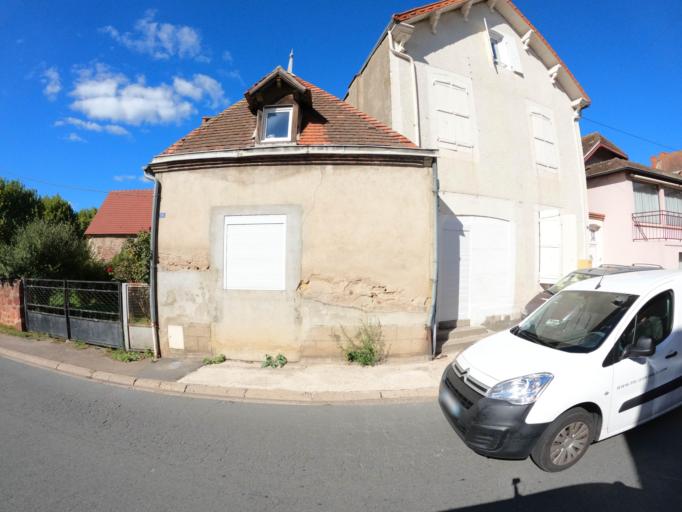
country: FR
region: Auvergne
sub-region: Departement de l'Allier
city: Doyet
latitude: 46.3970
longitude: 2.8558
